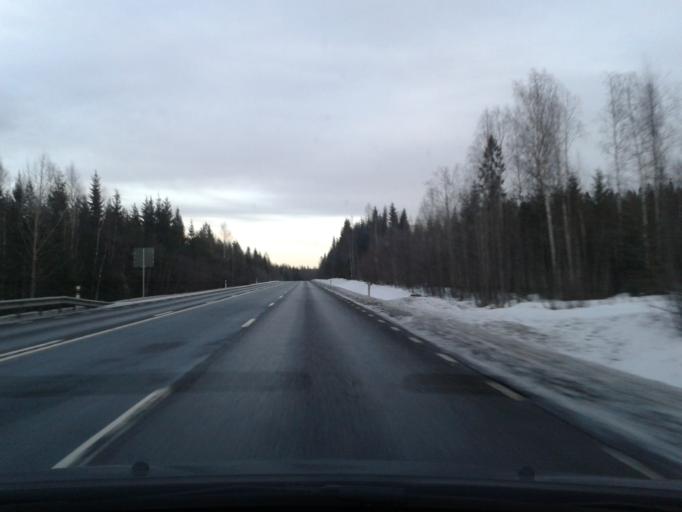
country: SE
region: Vaesternorrland
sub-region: Solleftea Kommun
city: Solleftea
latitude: 63.1414
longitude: 17.4209
